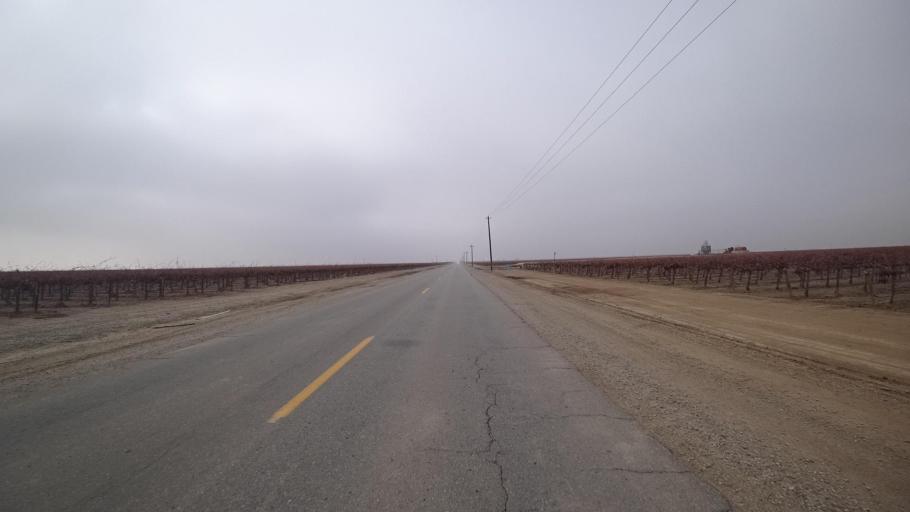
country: US
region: California
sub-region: Kern County
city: Maricopa
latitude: 35.0942
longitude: -119.1845
